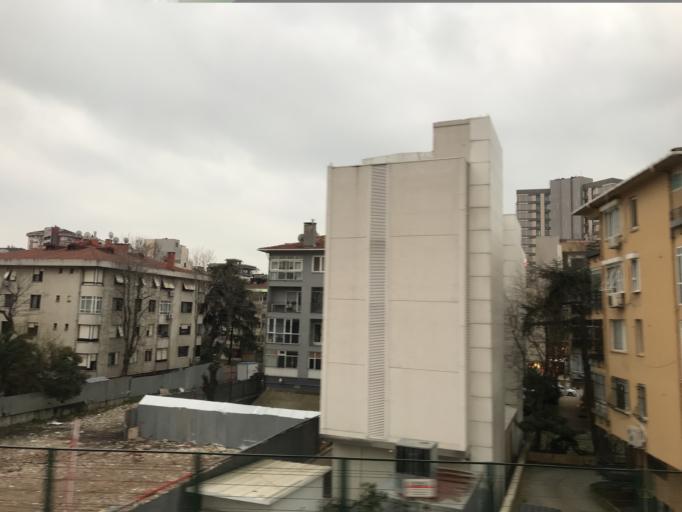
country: TR
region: Istanbul
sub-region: Atasehir
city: Atasehir
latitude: 40.9610
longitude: 29.0810
